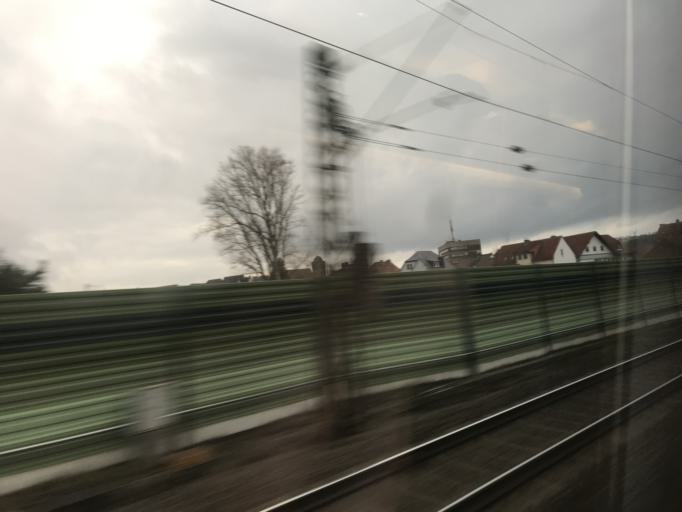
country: DE
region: Hesse
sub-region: Regierungsbezirk Kassel
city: Bad Hersfeld
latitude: 50.8641
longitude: 9.7140
